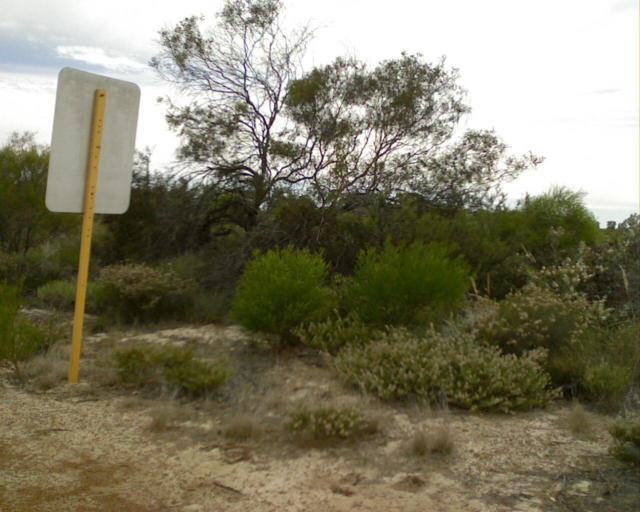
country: AU
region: Western Australia
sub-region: Dandaragan
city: Jurien Bay
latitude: -29.8154
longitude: 115.2756
